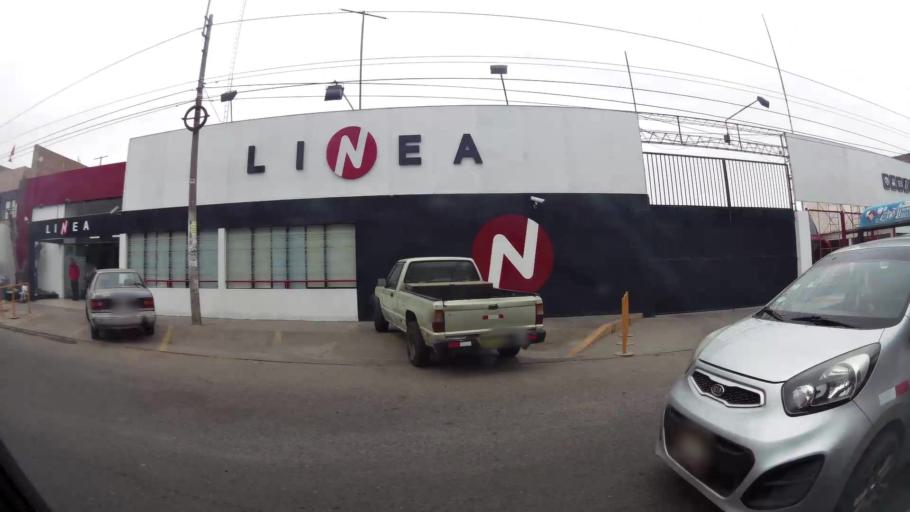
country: PE
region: La Libertad
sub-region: Provincia de Trujillo
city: Trujillo
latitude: -8.1264
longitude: -79.0278
